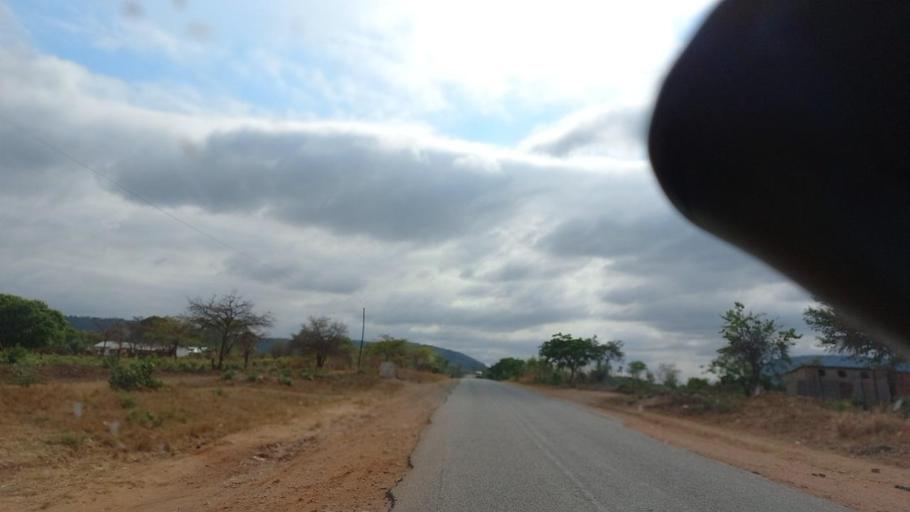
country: ZM
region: Lusaka
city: Chongwe
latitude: -15.1340
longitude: 29.4426
